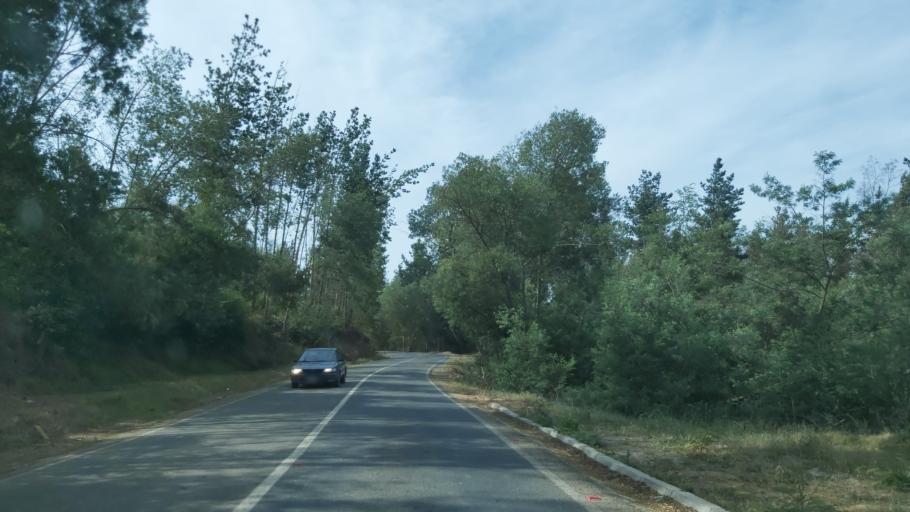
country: CL
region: Maule
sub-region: Provincia de Talca
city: Constitucion
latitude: -34.8538
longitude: -72.0329
